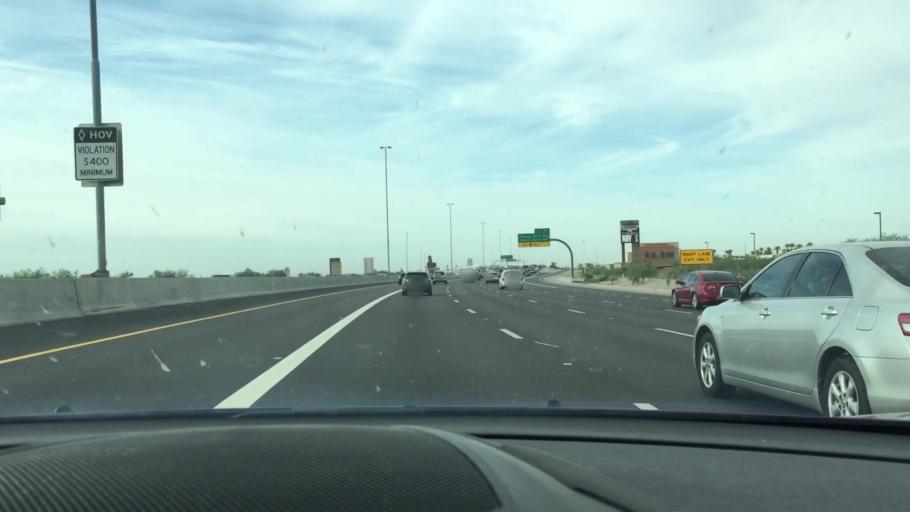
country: US
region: Arizona
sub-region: Maricopa County
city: Scottsdale
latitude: 33.5455
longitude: -111.8798
